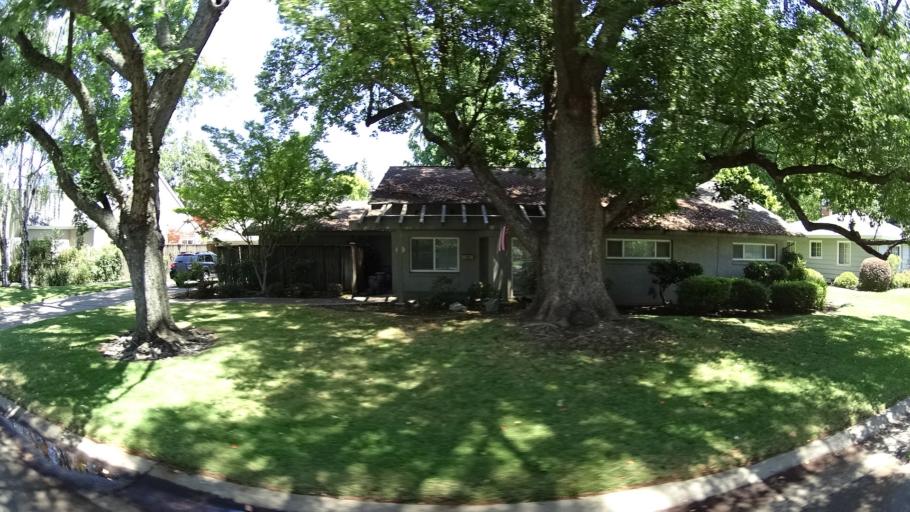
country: US
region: California
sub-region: Yolo County
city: West Sacramento
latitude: 38.5298
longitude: -121.5217
